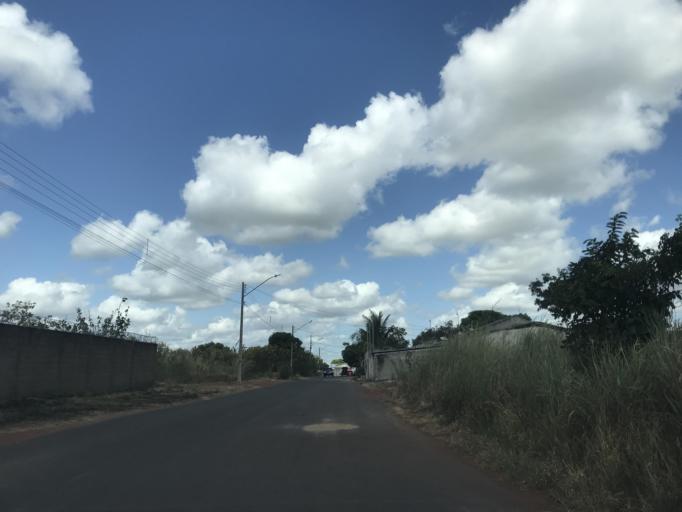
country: BR
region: Goias
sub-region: Luziania
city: Luziania
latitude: -16.2566
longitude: -47.9744
